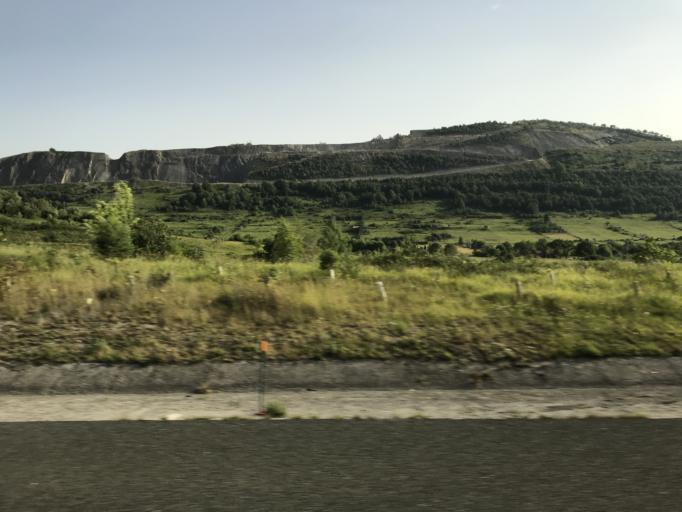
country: ES
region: Navarre
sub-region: Provincia de Navarra
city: Altsasu
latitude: 42.9162
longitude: -2.1927
